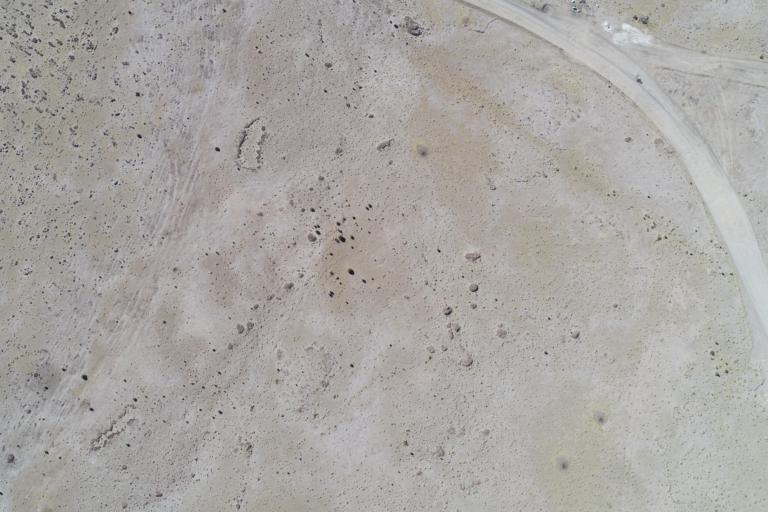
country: BO
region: Potosi
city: Colchani
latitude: -20.3516
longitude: -66.9031
